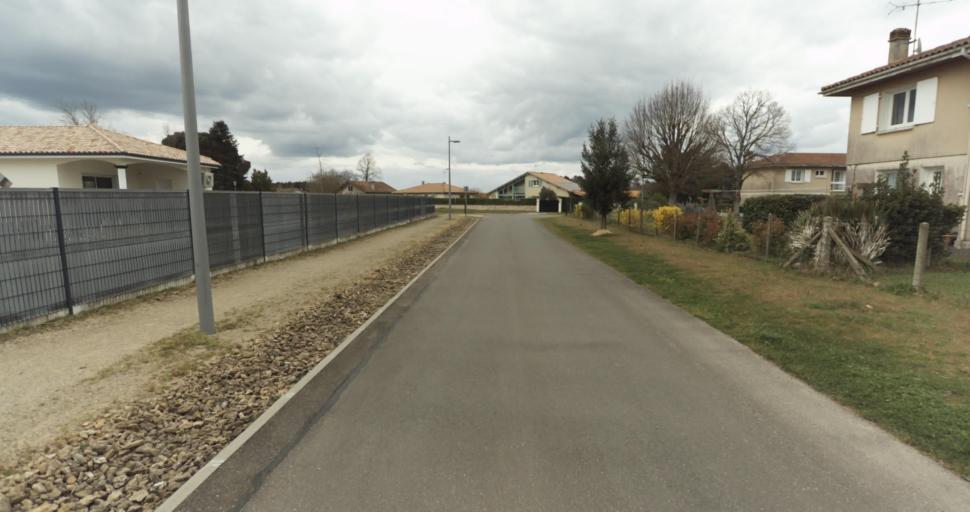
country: FR
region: Aquitaine
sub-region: Departement des Landes
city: Sarbazan
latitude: 44.0200
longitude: -0.3129
